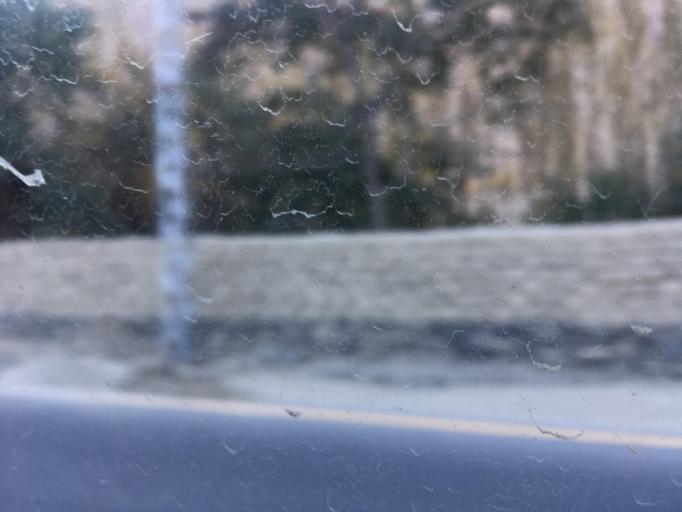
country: PK
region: Gilgit-Baltistan
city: Skardu
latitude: 35.3582
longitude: 75.5091
